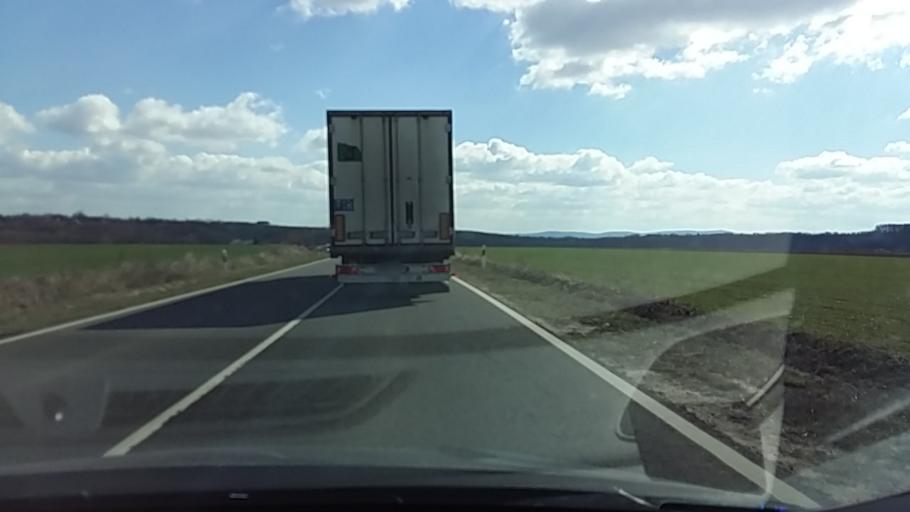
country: HU
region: Baranya
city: Kozarmisleny
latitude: 46.0331
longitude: 18.2736
